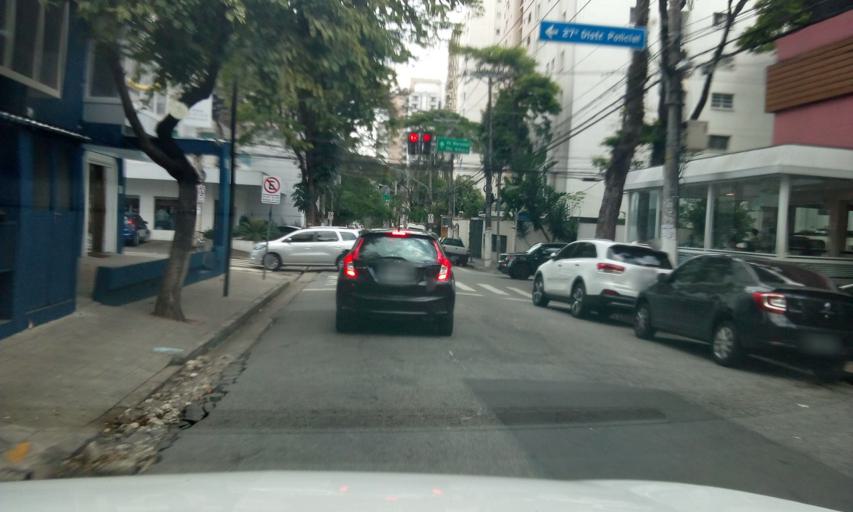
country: BR
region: Sao Paulo
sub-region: Sao Paulo
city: Sao Paulo
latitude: -23.6120
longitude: -46.6790
